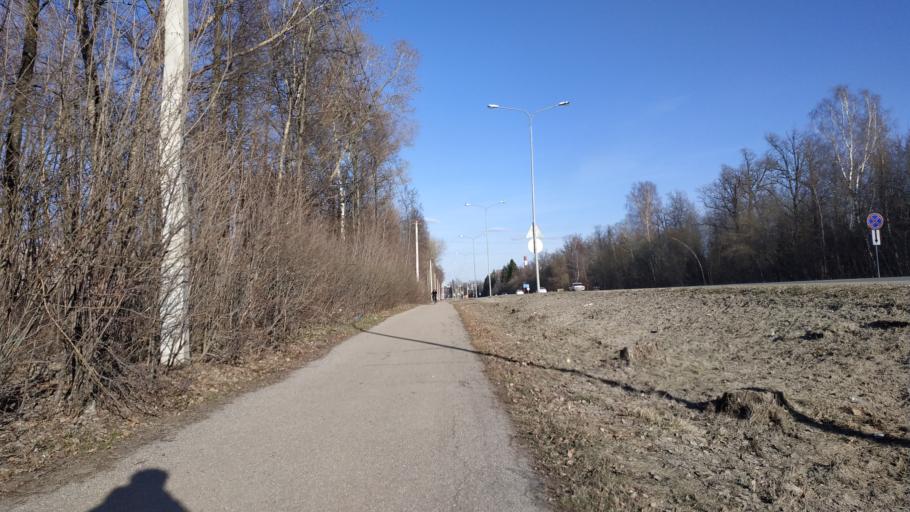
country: RU
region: Chuvashia
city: Novyye Lapsary
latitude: 56.1310
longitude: 47.1484
